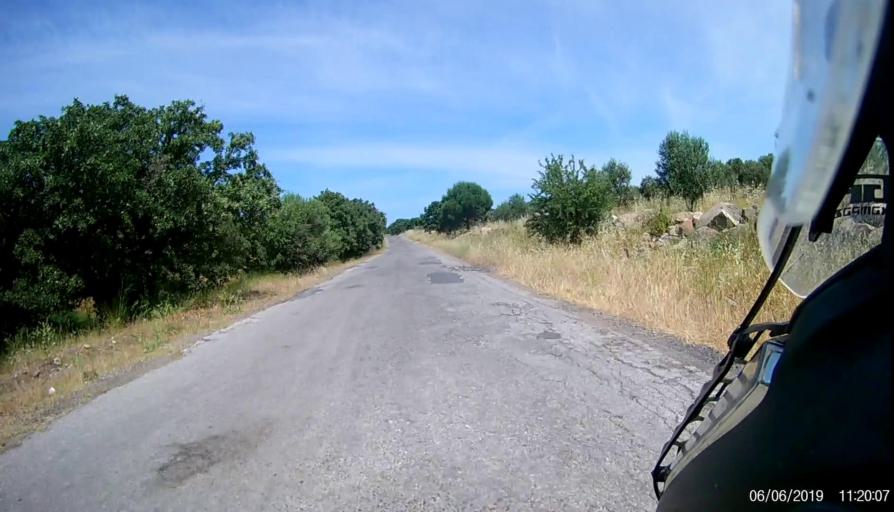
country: TR
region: Canakkale
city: Gulpinar
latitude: 39.6632
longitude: 26.1638
